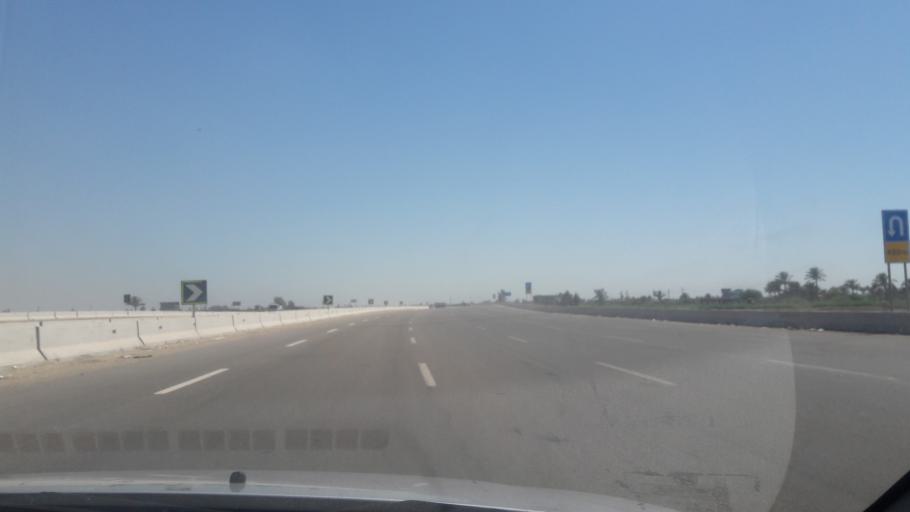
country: EG
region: Muhafazat Bur Sa`id
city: Port Said
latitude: 31.1078
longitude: 32.2337
